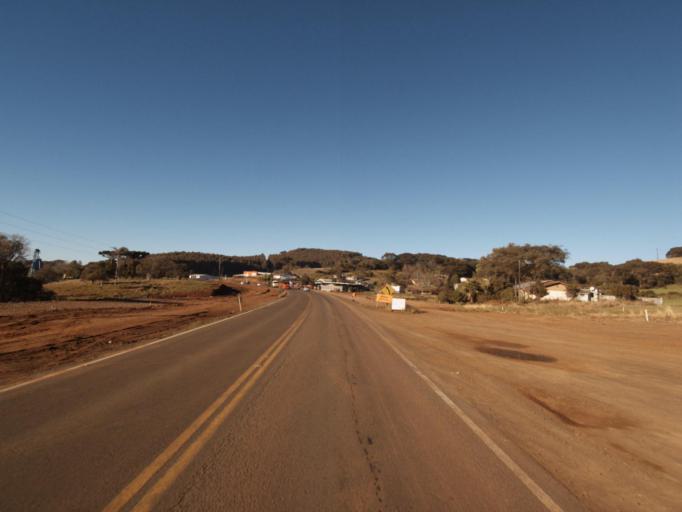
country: AR
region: Misiones
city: Bernardo de Irigoyen
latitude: -26.4571
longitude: -53.5105
